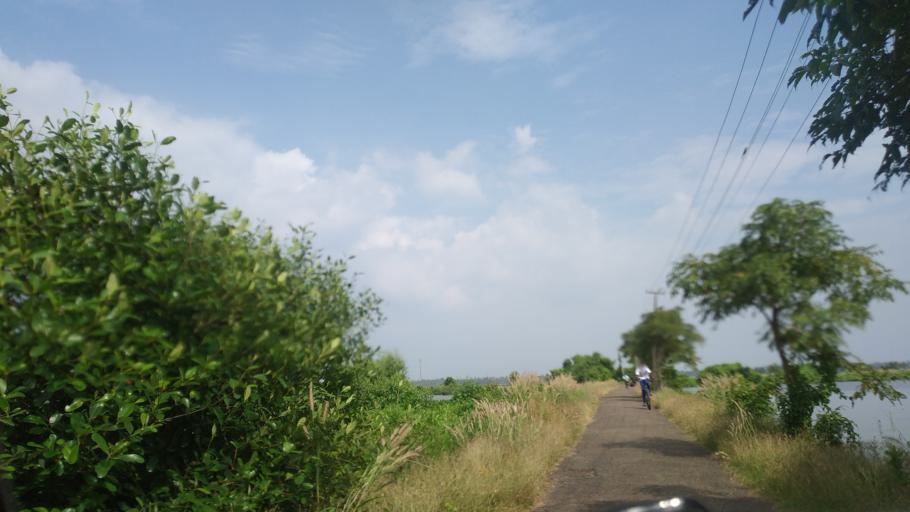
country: IN
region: Kerala
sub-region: Ernakulam
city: Elur
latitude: 10.0866
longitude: 76.2169
